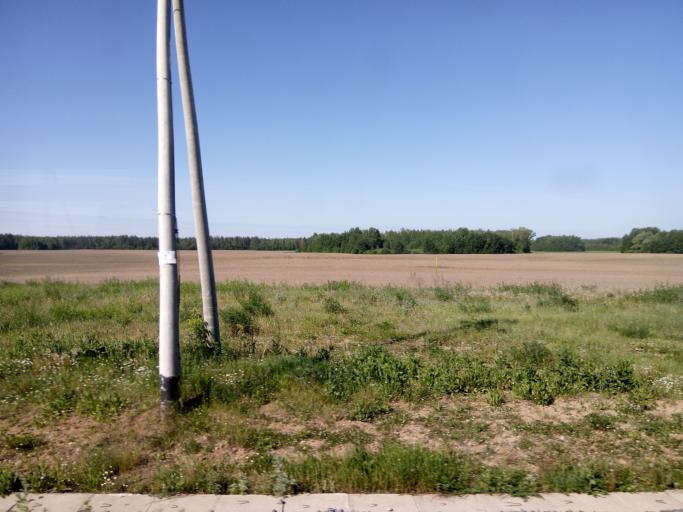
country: RU
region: Tatarstan
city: Stolbishchi
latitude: 55.6787
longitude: 49.2068
